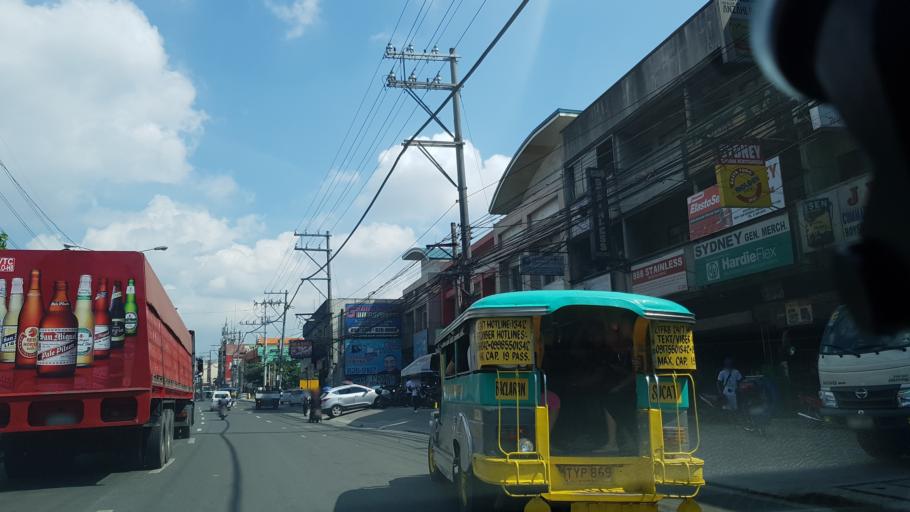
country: PH
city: Sambayanihan People's Village
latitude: 14.4756
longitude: 121.0005
